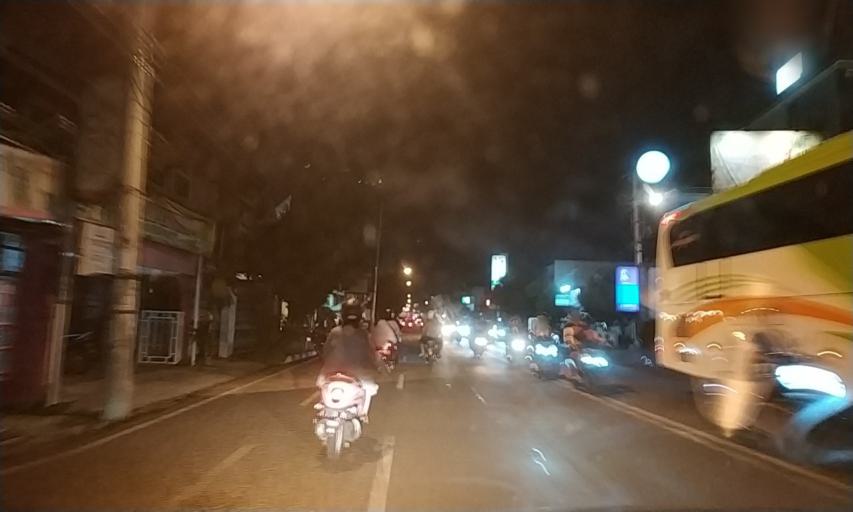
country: ID
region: Daerah Istimewa Yogyakarta
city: Yogyakarta
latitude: -7.7956
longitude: 110.3529
